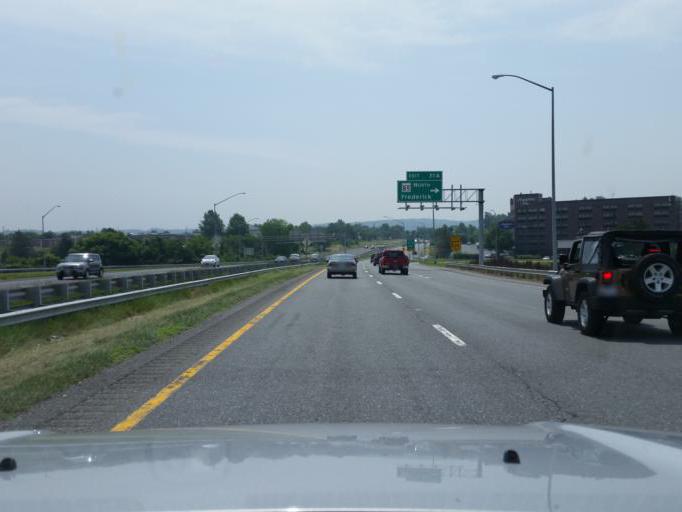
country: US
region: Maryland
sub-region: Frederick County
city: Ballenger Creek
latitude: 39.3813
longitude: -77.4092
